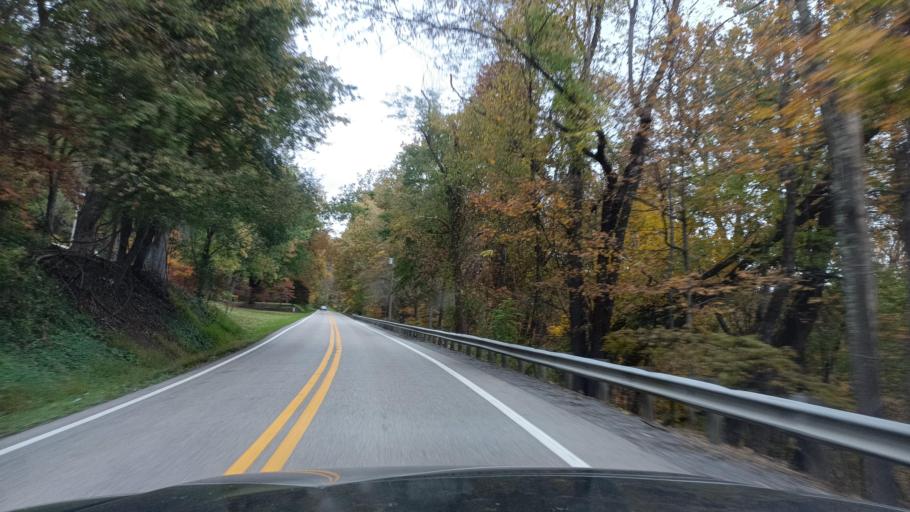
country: US
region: West Virginia
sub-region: Taylor County
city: Grafton
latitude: 39.3675
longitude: -79.9735
